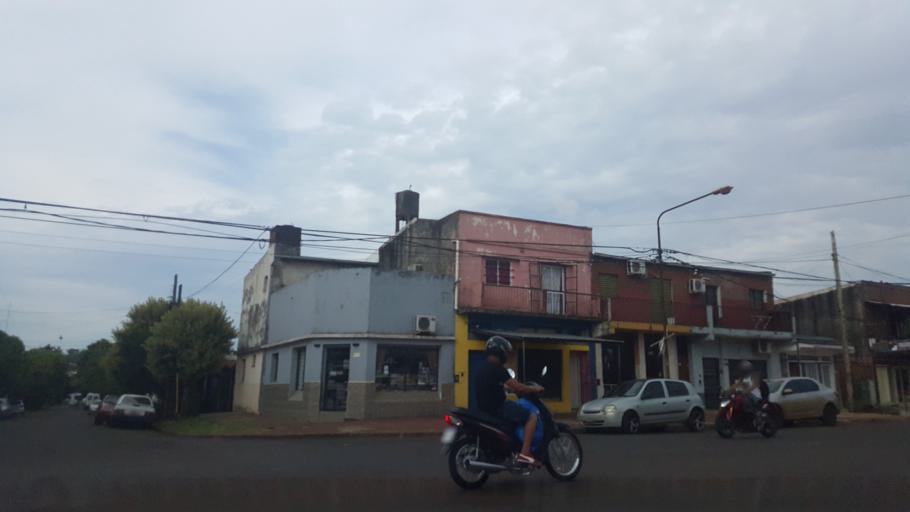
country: AR
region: Misiones
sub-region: Departamento de Capital
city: Posadas
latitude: -27.3845
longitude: -55.8990
